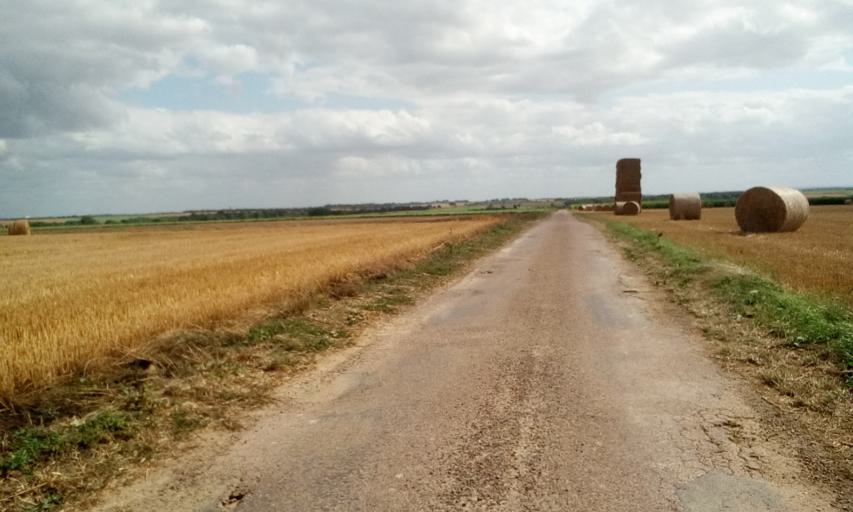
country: FR
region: Lower Normandy
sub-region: Departement du Calvados
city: Ver-sur-Mer
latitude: 49.3031
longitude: -0.5075
